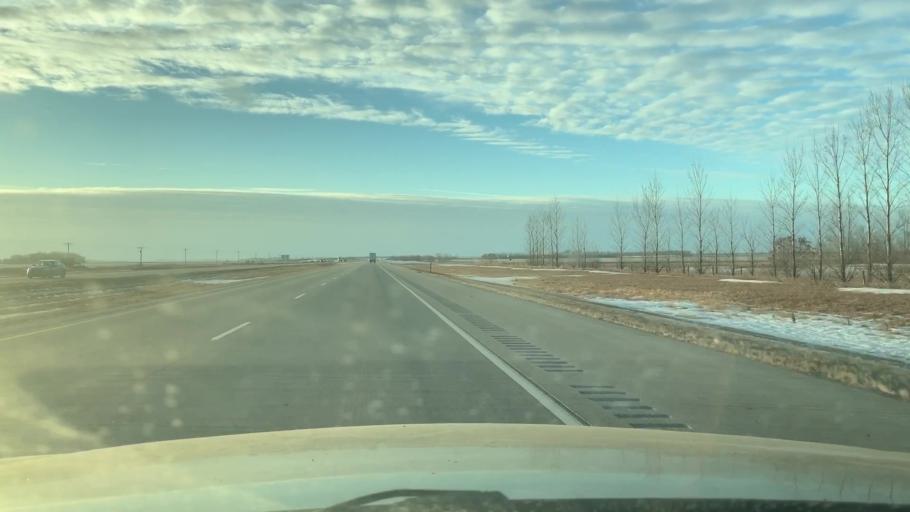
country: US
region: North Dakota
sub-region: Cass County
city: Casselton
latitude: 46.8756
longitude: -97.3214
